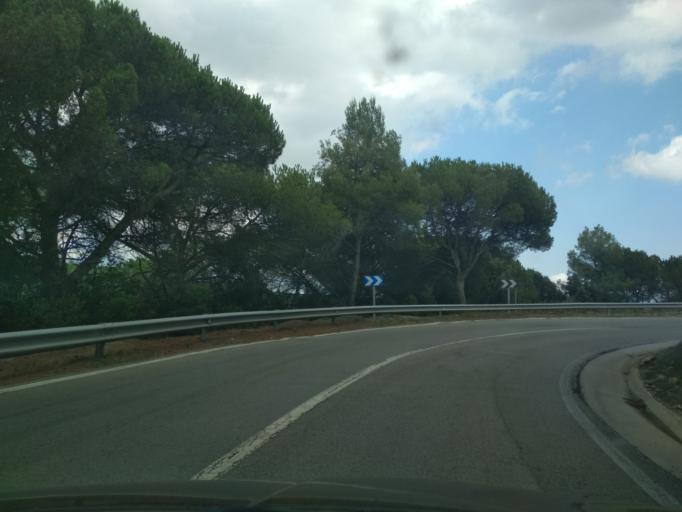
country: ES
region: Catalonia
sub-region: Provincia de Barcelona
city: Sant Feliu de Codines
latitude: 41.7043
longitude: 2.1641
